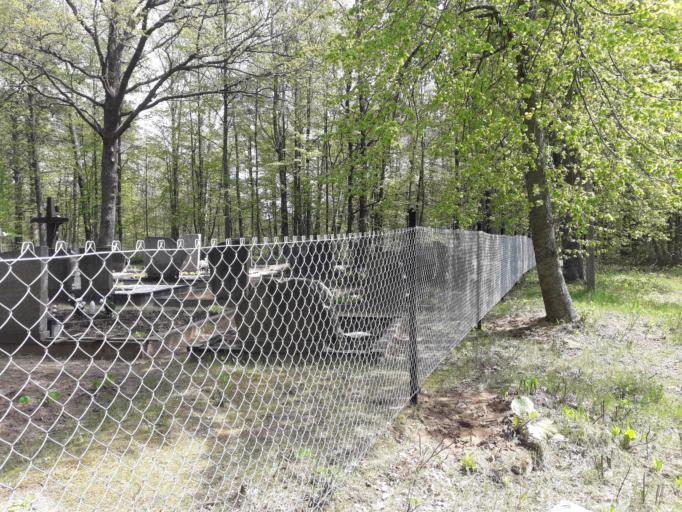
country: LT
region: Alytaus apskritis
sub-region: Alytaus rajonas
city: Daugai
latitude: 54.2167
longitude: 24.2228
